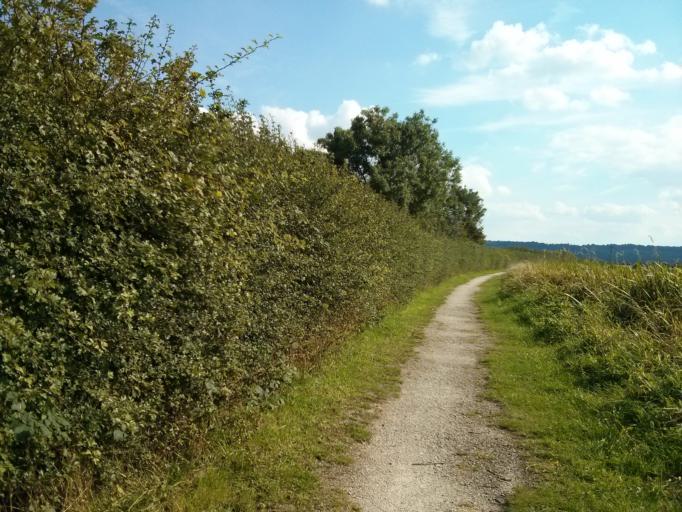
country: GB
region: England
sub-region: Lincolnshire
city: Long Bennington
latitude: 52.9138
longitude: -0.8261
